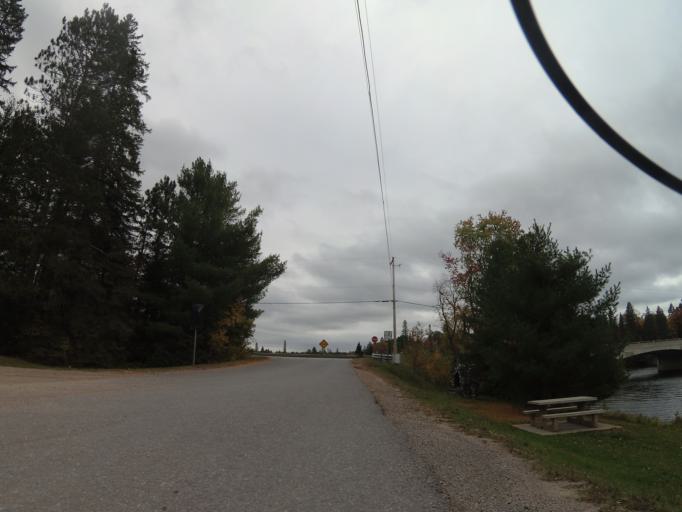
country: CA
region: Ontario
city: Renfrew
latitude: 45.2505
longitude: -77.1858
